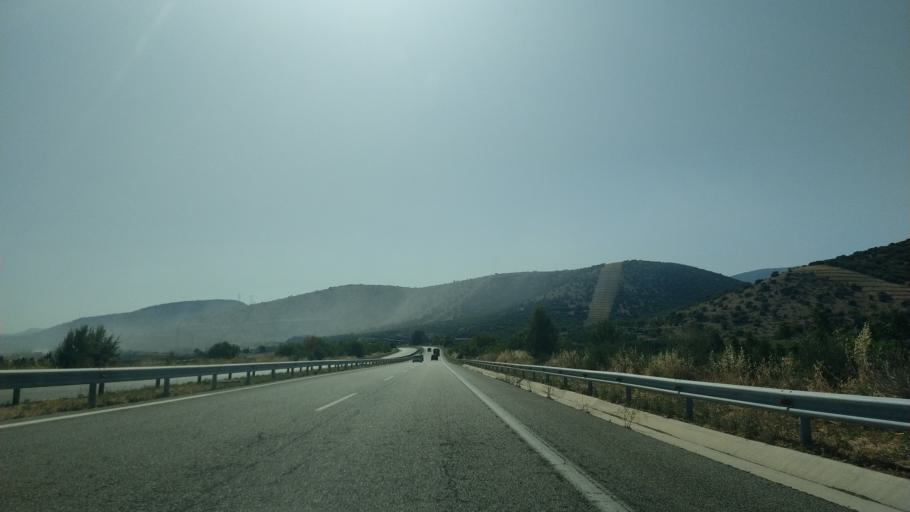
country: GR
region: East Macedonia and Thrace
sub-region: Nomos Kavalas
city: Nea Karvali
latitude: 40.9703
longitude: 24.4999
